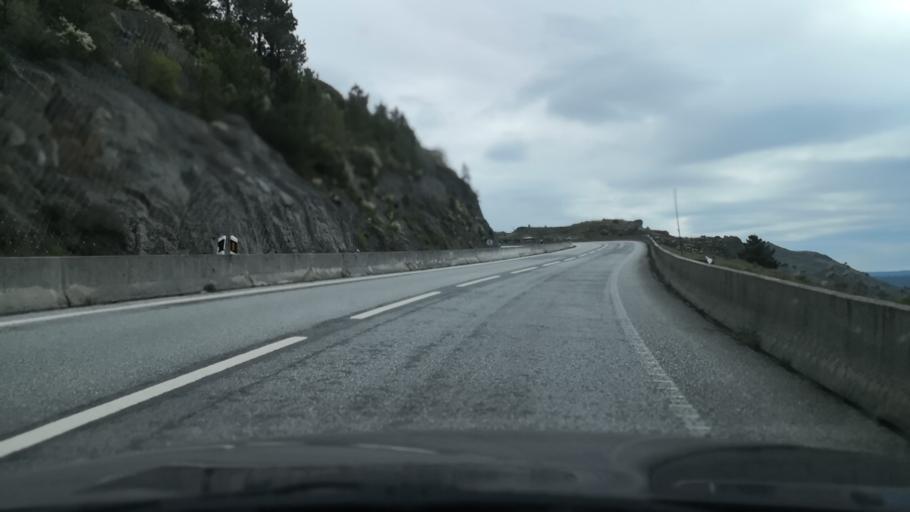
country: PT
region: Guarda
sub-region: Guarda
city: Guarda
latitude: 40.5934
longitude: -7.2746
